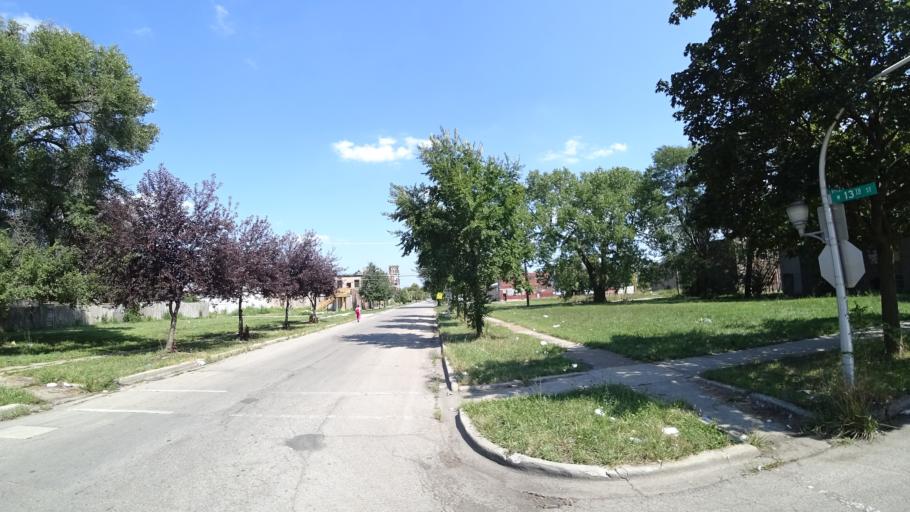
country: US
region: Illinois
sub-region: Cook County
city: Cicero
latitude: 41.8642
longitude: -87.7264
